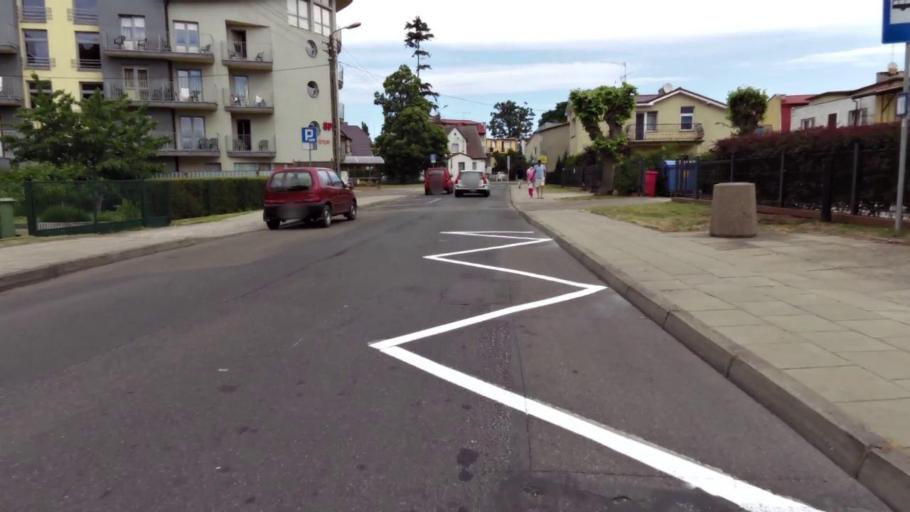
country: PL
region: West Pomeranian Voivodeship
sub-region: Powiat kamienski
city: Miedzyzdroje
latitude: 53.9262
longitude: 14.4400
